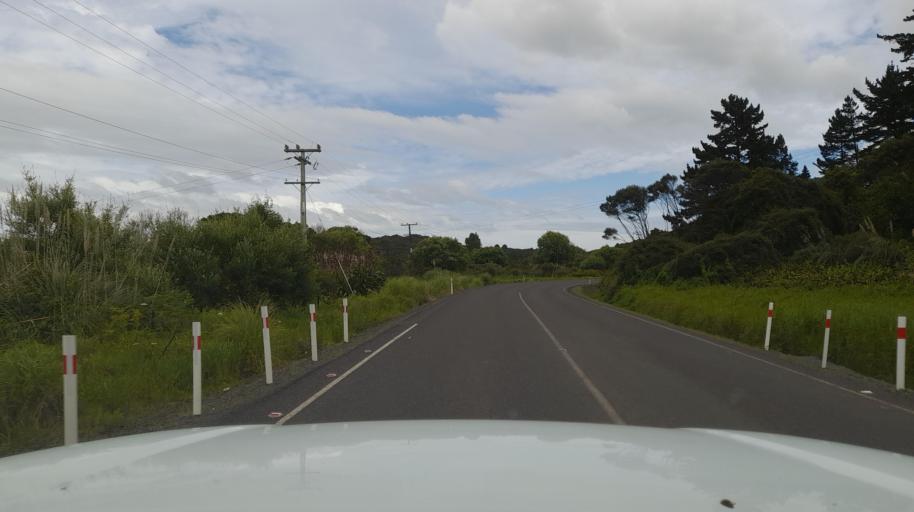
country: NZ
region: Northland
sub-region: Far North District
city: Kaitaia
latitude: -35.3873
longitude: 173.3835
